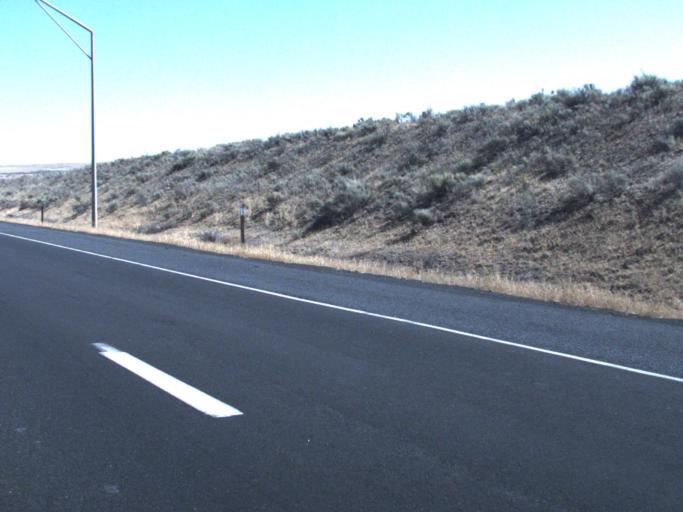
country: US
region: Washington
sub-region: Adams County
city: Ritzville
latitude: 47.0967
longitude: -118.6587
